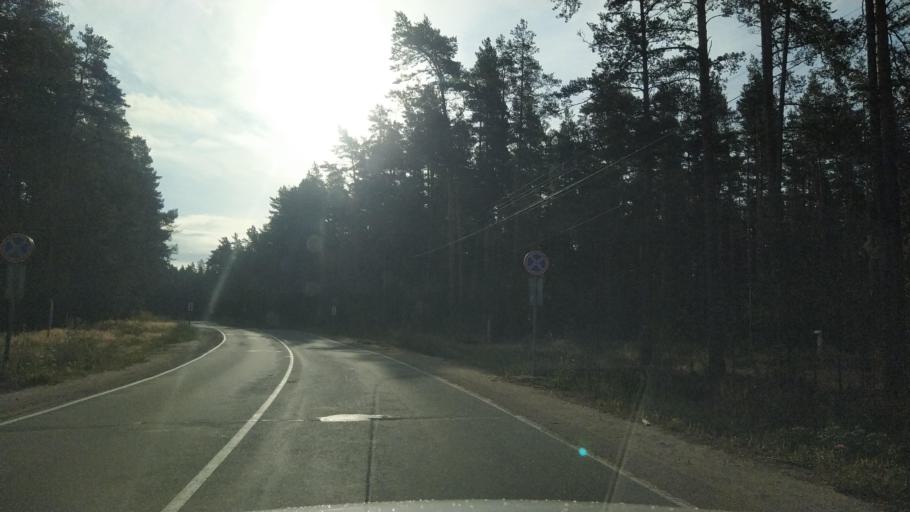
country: RU
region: Leningrad
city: Priozersk
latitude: 61.0014
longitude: 30.1996
